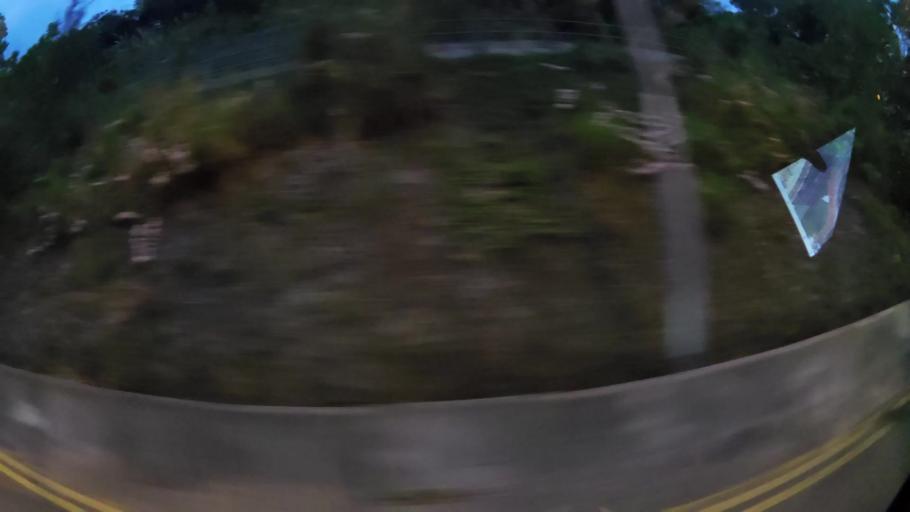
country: HK
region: Sha Tin
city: Sha Tin
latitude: 22.3693
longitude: 114.1717
